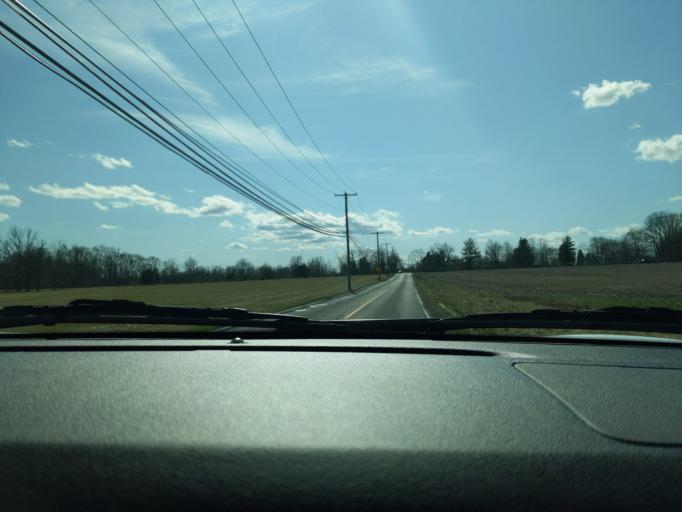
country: US
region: Pennsylvania
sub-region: Bucks County
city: Richlandtown
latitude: 40.4550
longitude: -75.2987
